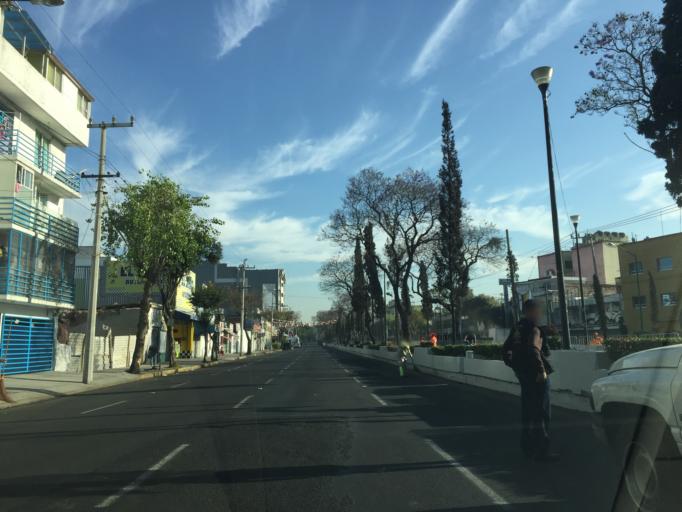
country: MX
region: Mexico City
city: Cuauhtemoc
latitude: 19.4543
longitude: -99.1297
